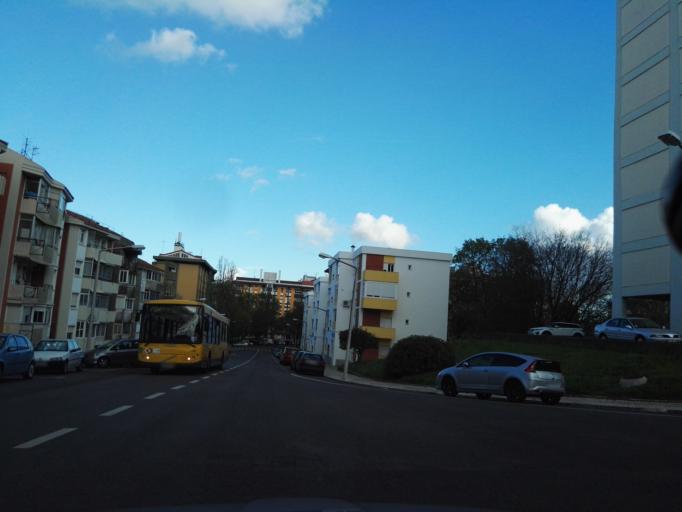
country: PT
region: Lisbon
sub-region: Loures
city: Moscavide
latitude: 38.7654
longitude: -9.1159
